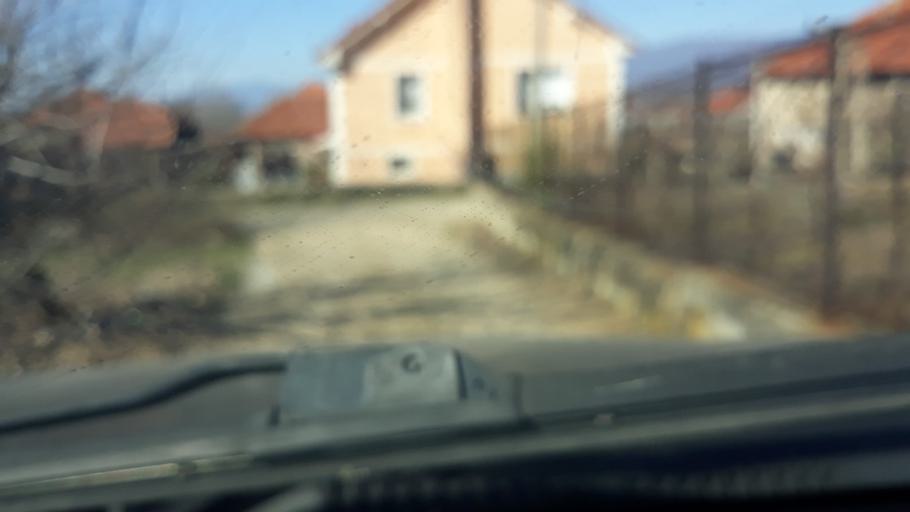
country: MK
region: Novo Selo
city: Susica
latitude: 41.3800
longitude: 22.8175
